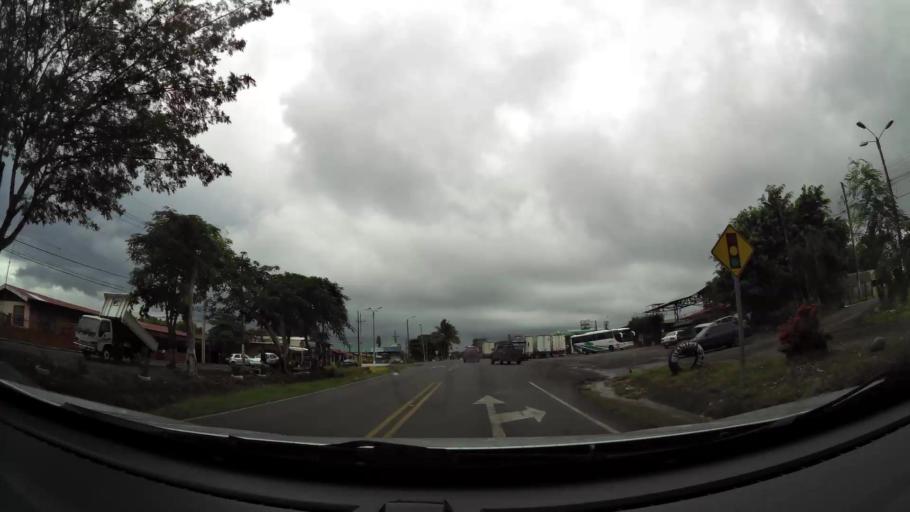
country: CR
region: Puntarenas
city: Esparza
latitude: 9.9952
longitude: -84.6670
